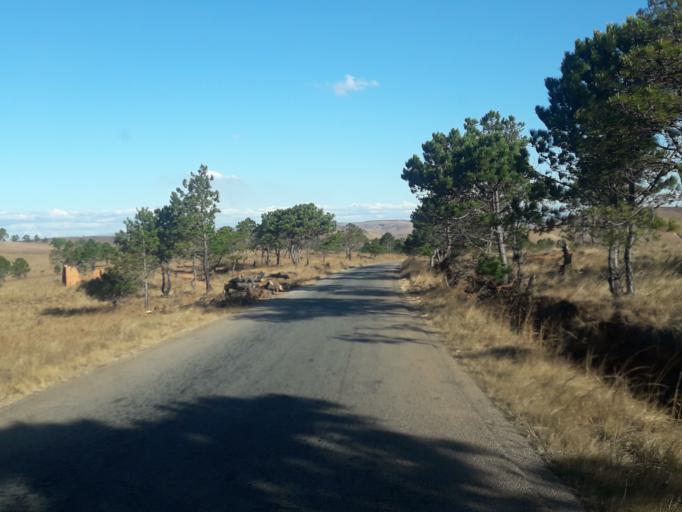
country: MG
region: Analamanga
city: Ankazobe
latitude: -17.8963
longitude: 47.0886
